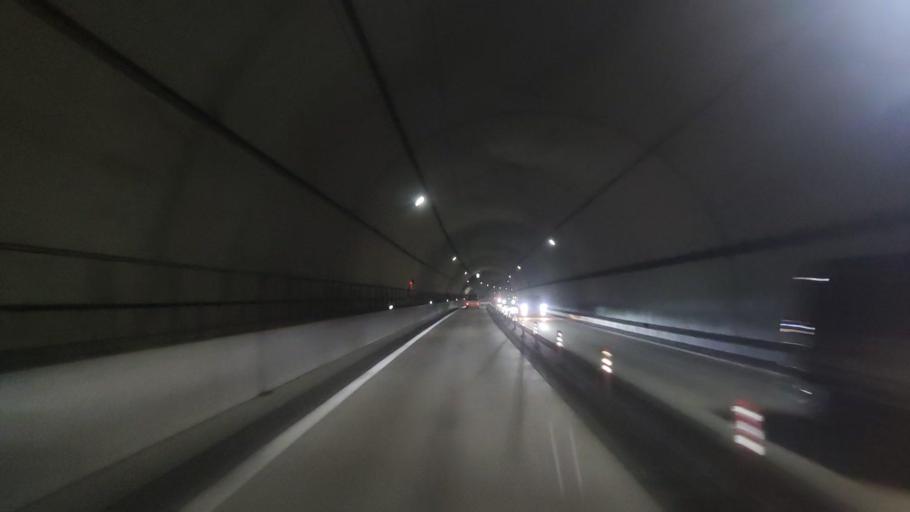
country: JP
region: Wakayama
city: Tanabe
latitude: 33.5882
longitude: 135.4434
